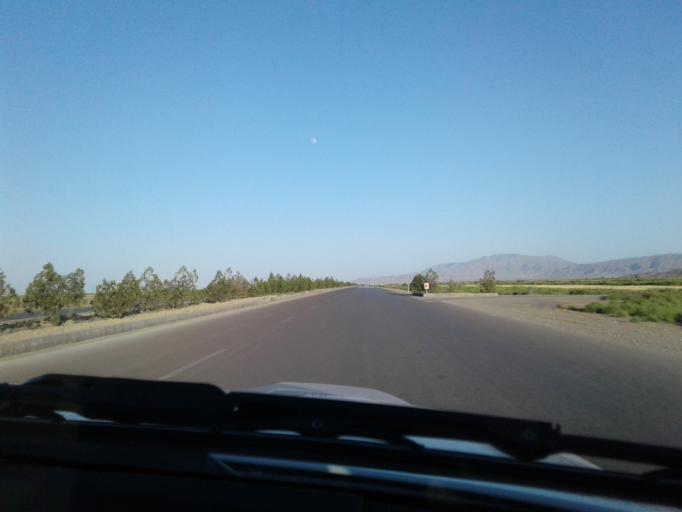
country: TM
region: Ahal
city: Baharly
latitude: 38.3675
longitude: 57.5216
